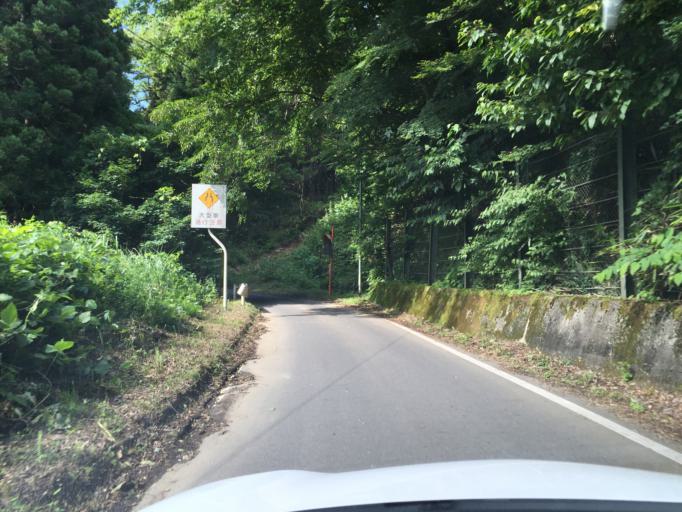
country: JP
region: Fukushima
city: Ishikawa
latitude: 37.1169
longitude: 140.6565
